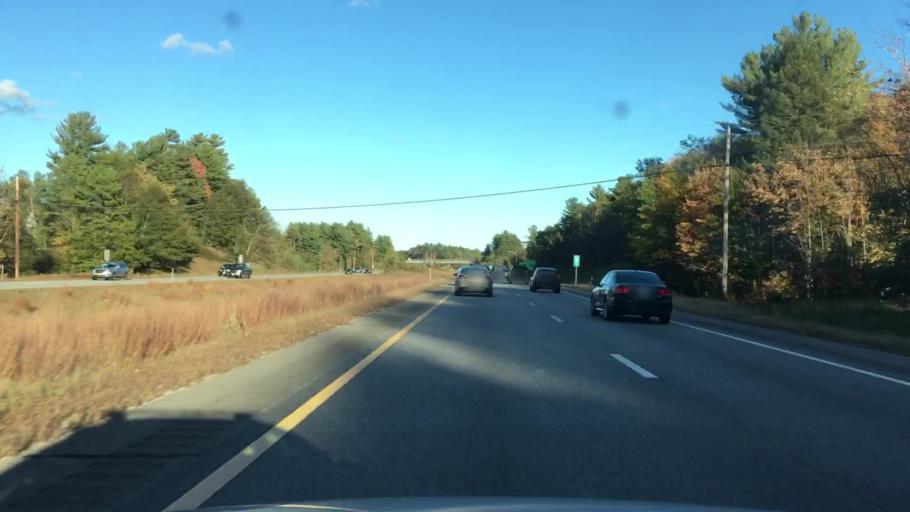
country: US
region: New Hampshire
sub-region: Rockingham County
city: Raymond
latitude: 43.0231
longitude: -71.2056
